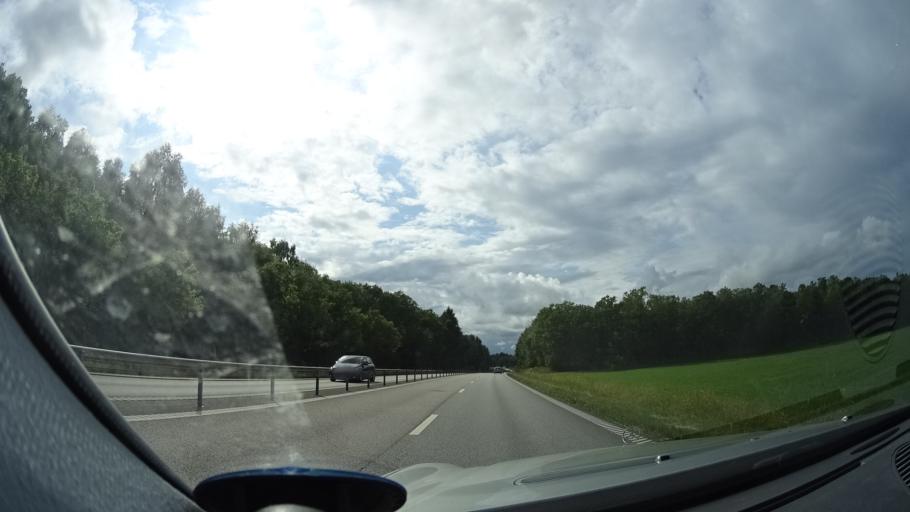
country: SE
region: Blekinge
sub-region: Karlshamns Kommun
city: Karlshamn
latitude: 56.1880
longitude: 14.8101
